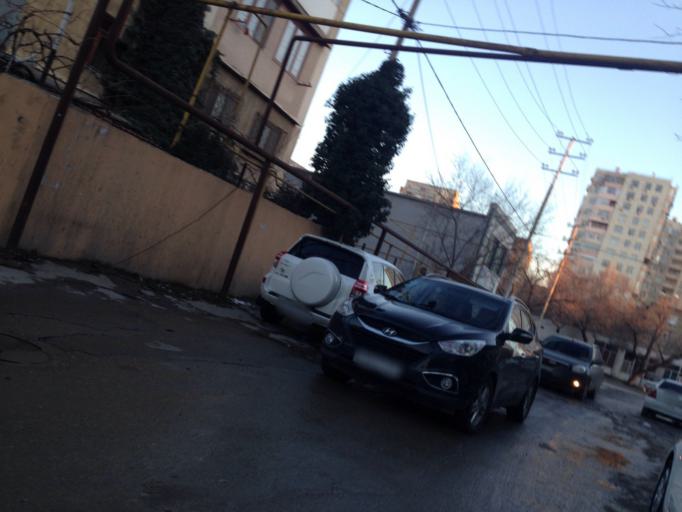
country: AZ
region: Baki
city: Baku
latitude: 40.4107
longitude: 49.8672
